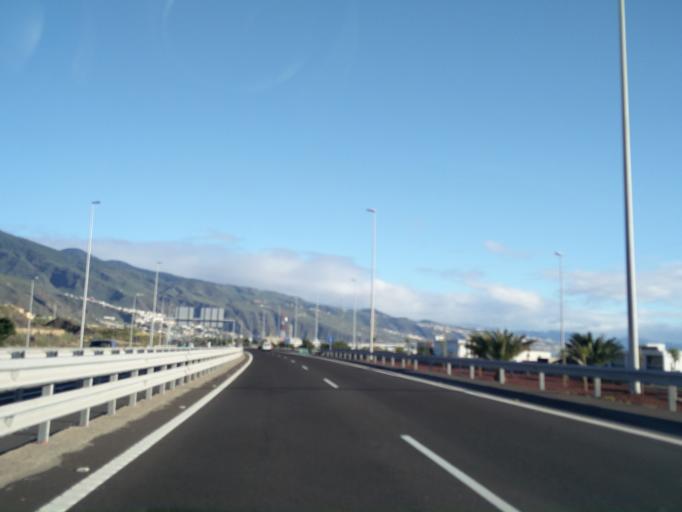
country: ES
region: Canary Islands
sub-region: Provincia de Santa Cruz de Tenerife
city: Candelaria
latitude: 28.3318
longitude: -16.3747
